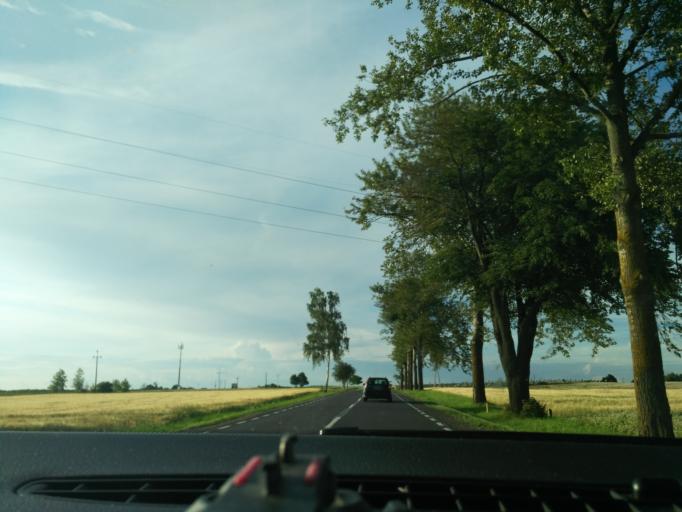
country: PL
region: Lublin Voivodeship
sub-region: Powiat krasnicki
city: Szastarka
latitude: 50.8135
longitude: 22.3193
